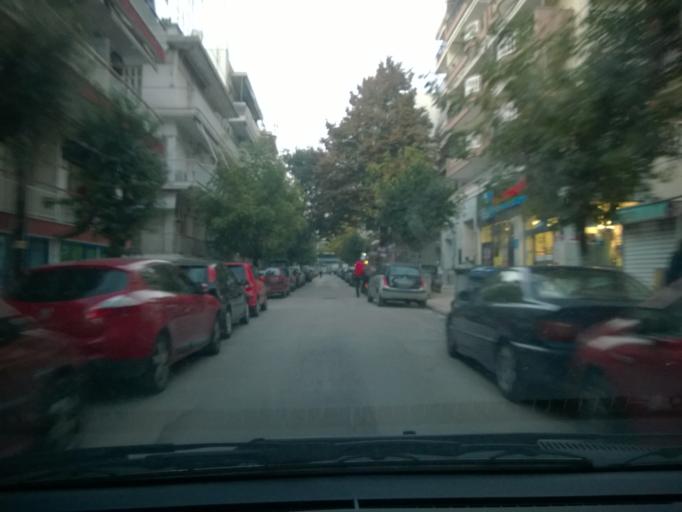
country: GR
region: Central Macedonia
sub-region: Nomos Thessalonikis
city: Ampelokipoi
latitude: 40.6554
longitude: 22.9226
